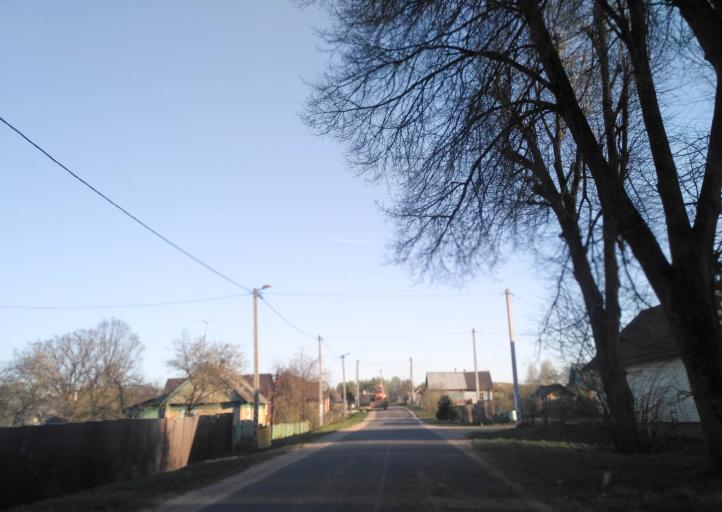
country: BY
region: Minsk
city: Pyatryshki
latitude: 54.1051
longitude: 27.1923
